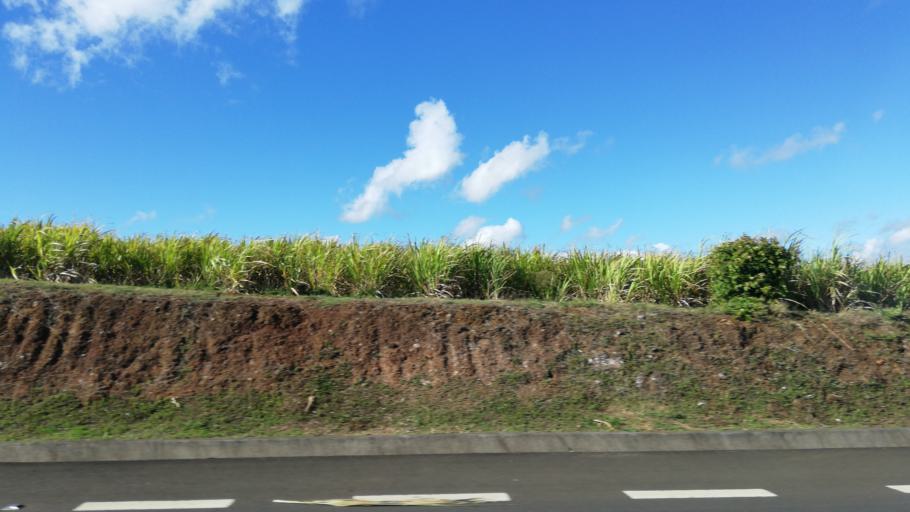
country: MU
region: Moka
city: Saint Pierre
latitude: -20.2320
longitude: 57.5219
